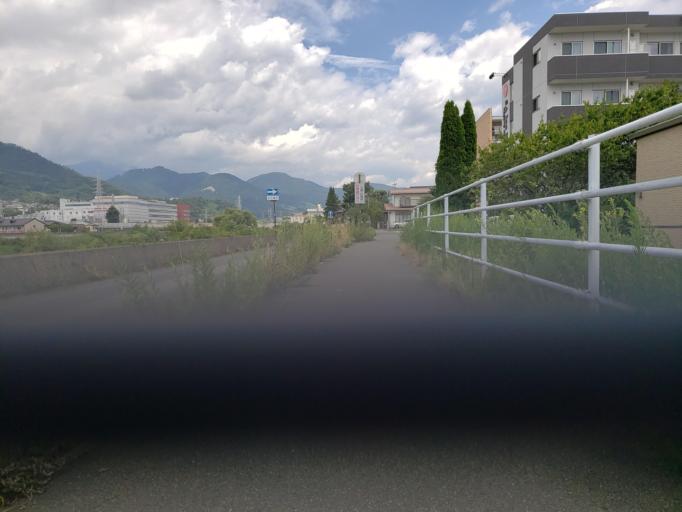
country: JP
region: Nagano
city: Nagano-shi
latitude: 36.6352
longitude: 138.1798
